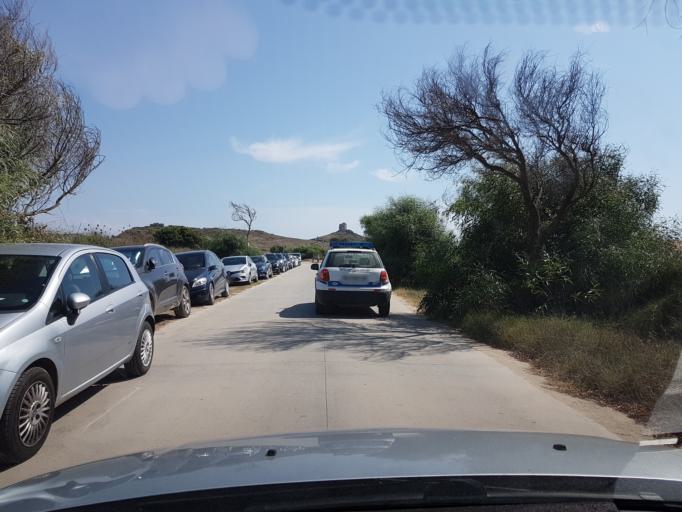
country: IT
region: Sardinia
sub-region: Provincia di Oristano
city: Cabras
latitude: 39.8819
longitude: 8.4393
